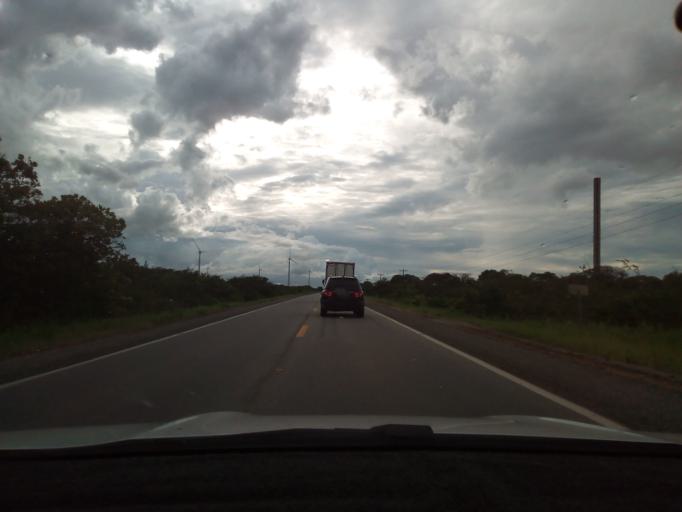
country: BR
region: Ceara
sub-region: Aracati
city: Aracati
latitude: -4.5930
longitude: -37.6871
